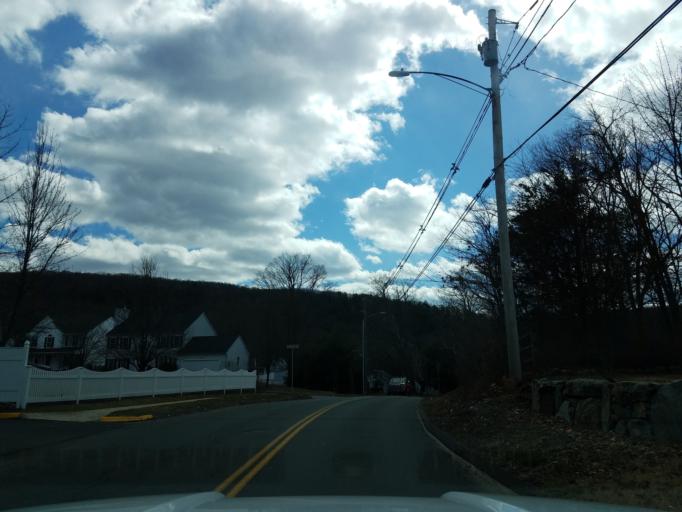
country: US
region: Connecticut
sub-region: New Haven County
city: Naugatuck
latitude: 41.4710
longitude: -73.0456
